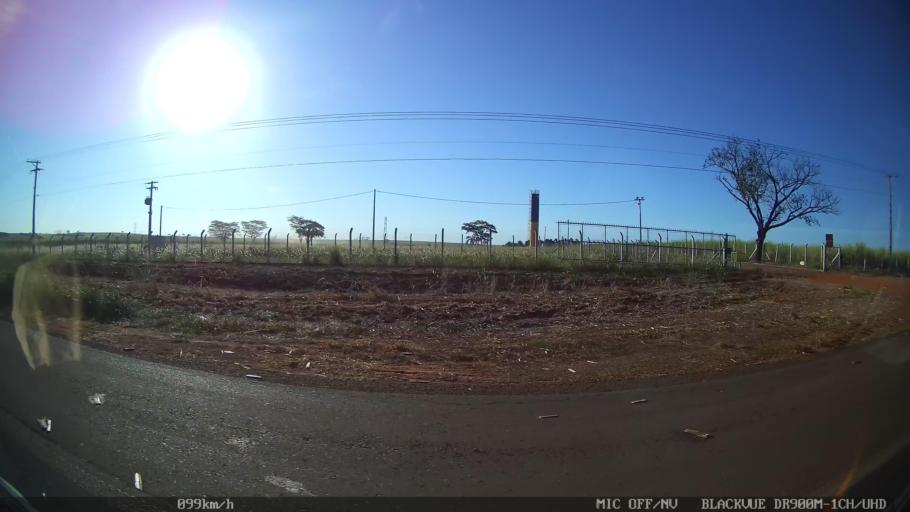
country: BR
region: Sao Paulo
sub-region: Olimpia
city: Olimpia
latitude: -20.7194
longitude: -49.0111
